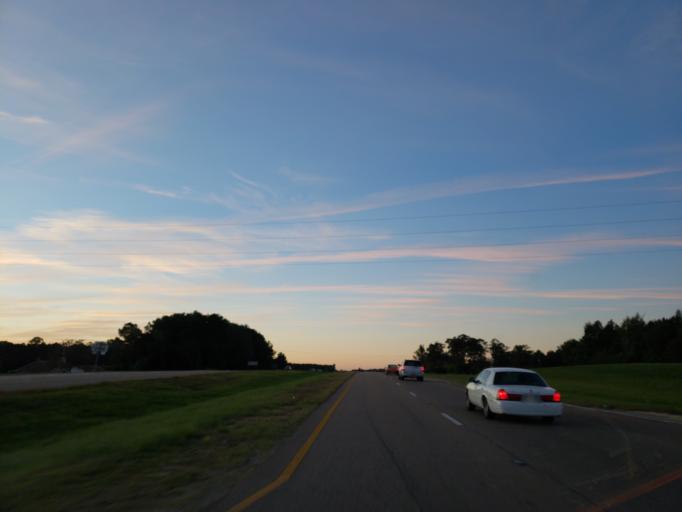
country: US
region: Mississippi
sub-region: Wayne County
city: Waynesboro
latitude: 31.7005
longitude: -88.6204
